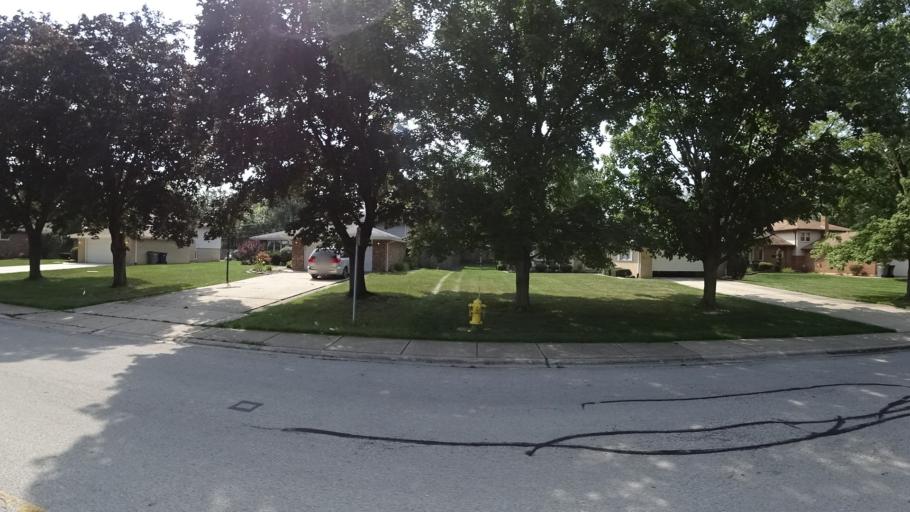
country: US
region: Illinois
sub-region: Cook County
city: Orland Park
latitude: 41.6157
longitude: -87.8642
